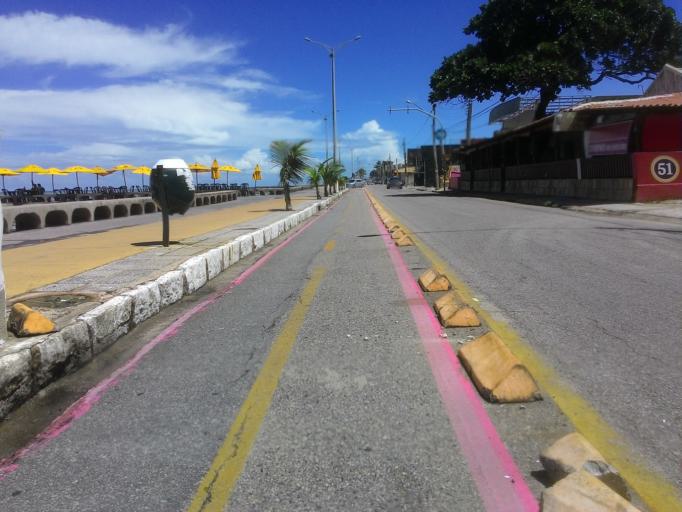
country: BR
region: Pernambuco
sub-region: Olinda
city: Olinda
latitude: -8.0070
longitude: -34.8407
